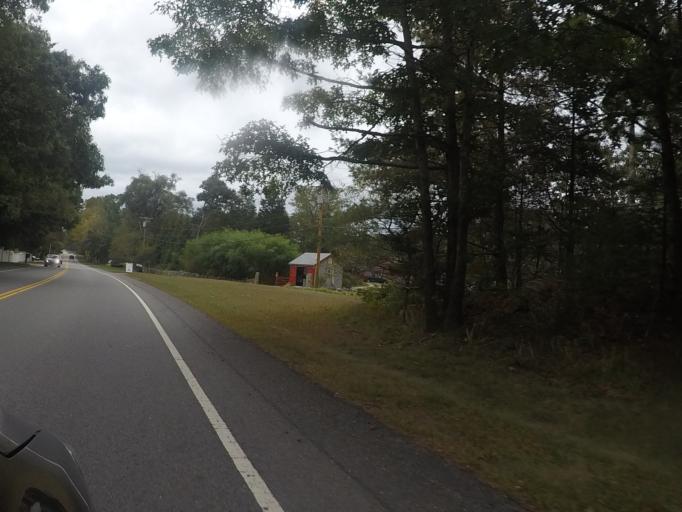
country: US
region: Massachusetts
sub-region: Bristol County
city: Smith Mills
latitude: 41.5970
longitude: -71.0025
